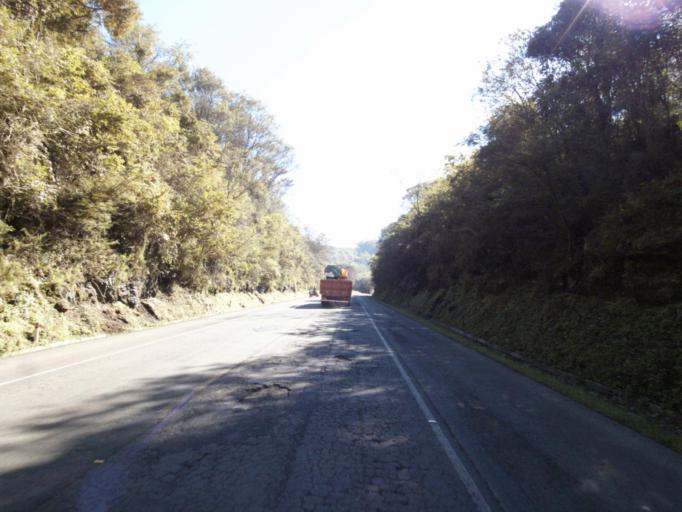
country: BR
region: Rio Grande do Sul
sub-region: Frederico Westphalen
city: Frederico Westphalen
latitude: -27.0513
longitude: -53.2293
